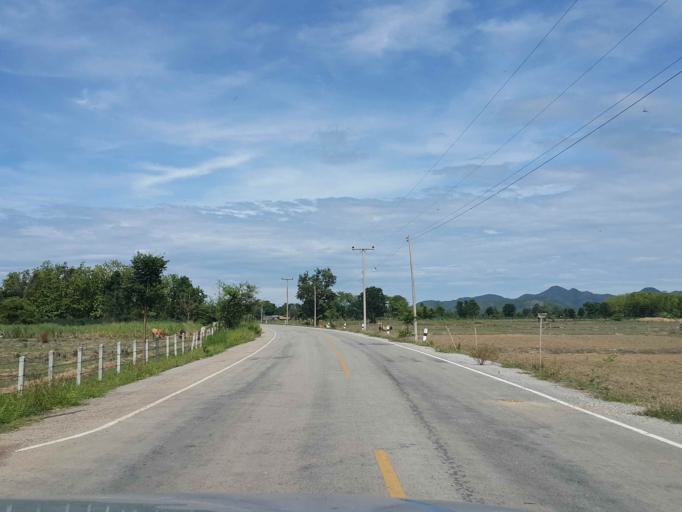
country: TH
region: Sukhothai
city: Ban Dan Lan Hoi
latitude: 17.1154
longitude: 99.5214
